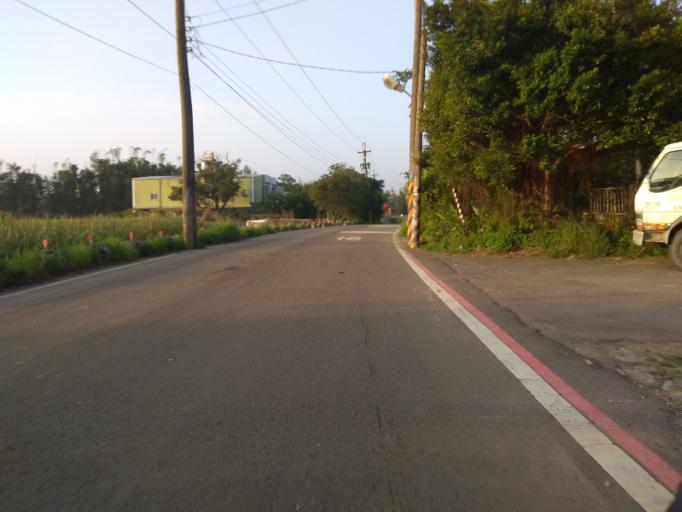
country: TW
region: Taiwan
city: Daxi
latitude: 24.9331
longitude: 121.2088
